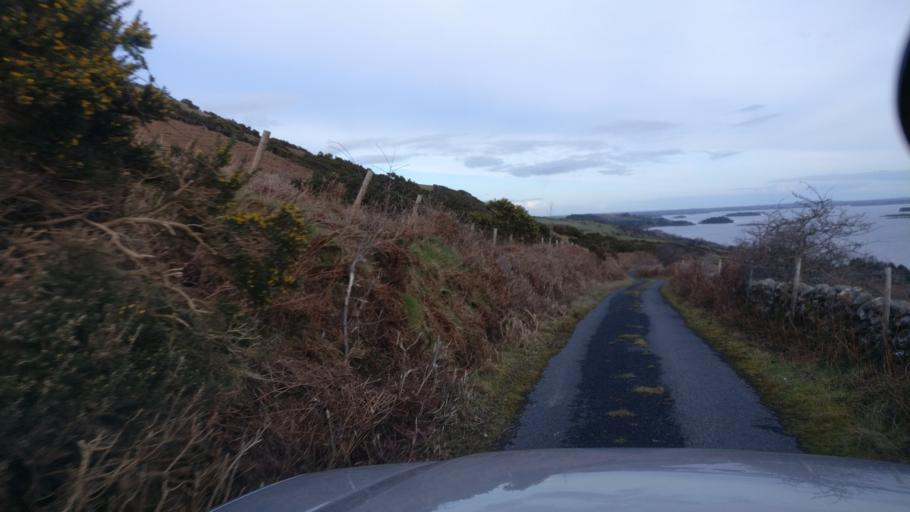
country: IE
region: Connaught
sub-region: County Galway
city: Oughterard
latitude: 53.5213
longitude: -9.4063
